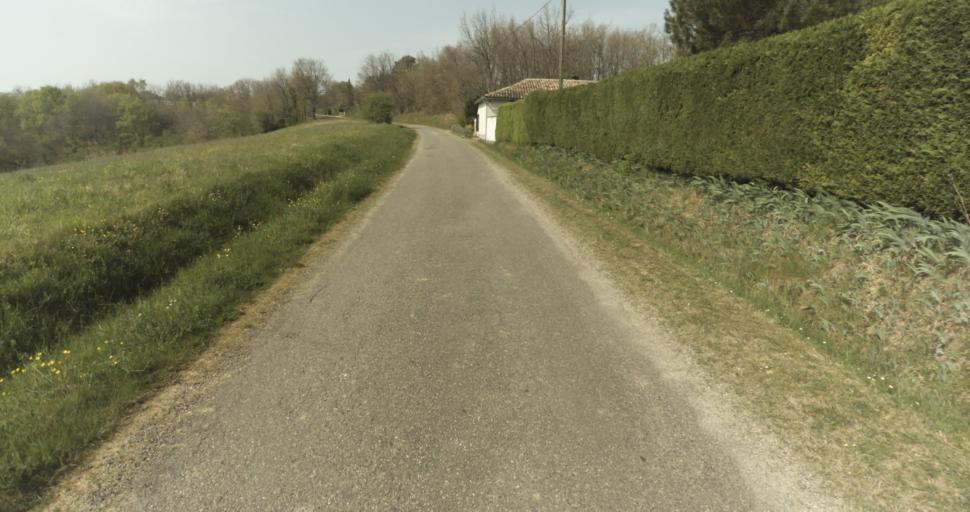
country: FR
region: Midi-Pyrenees
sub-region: Departement du Tarn-et-Garonne
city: Moissac
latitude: 44.1351
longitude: 1.1470
